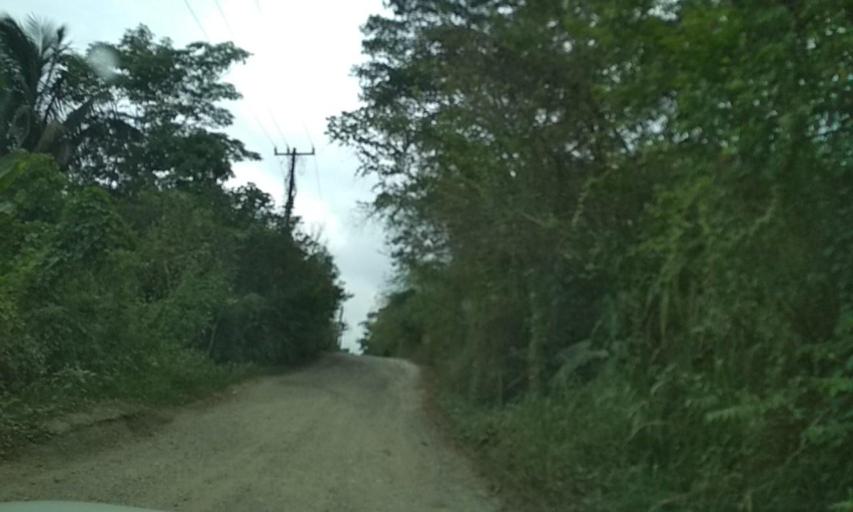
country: MX
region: Veracruz
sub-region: Uxpanapa
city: Poblado 10
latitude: 17.5026
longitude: -94.1533
